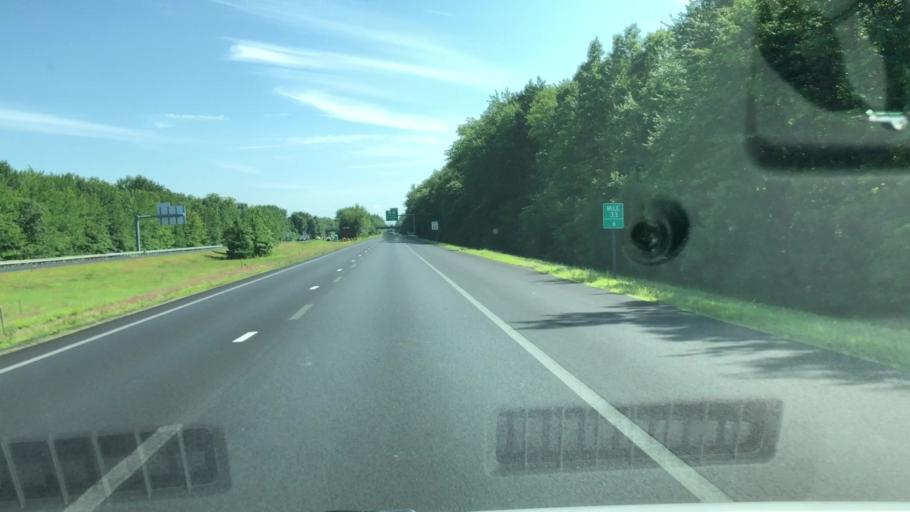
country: US
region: Massachusetts
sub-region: Franklin County
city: Whately
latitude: 42.4512
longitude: -72.6189
